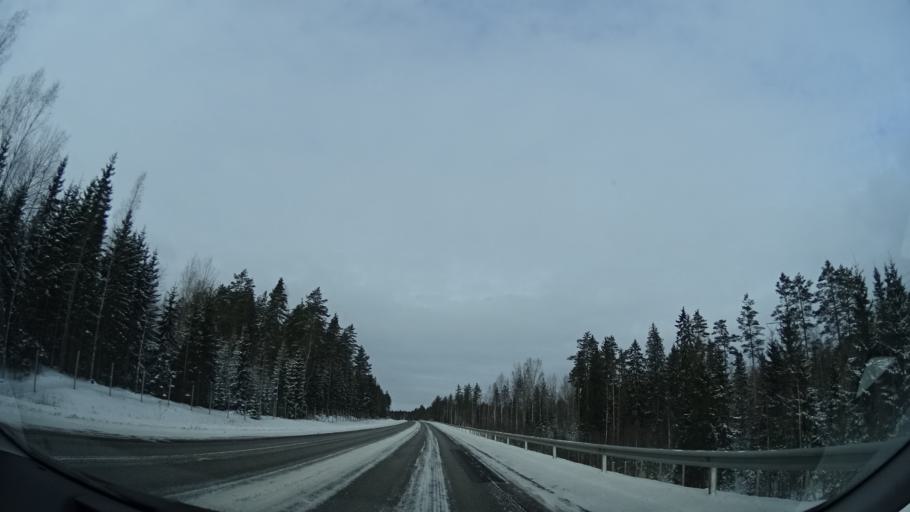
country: FI
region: Uusimaa
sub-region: Helsinki
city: Kaerkoelae
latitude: 60.6045
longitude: 24.0738
